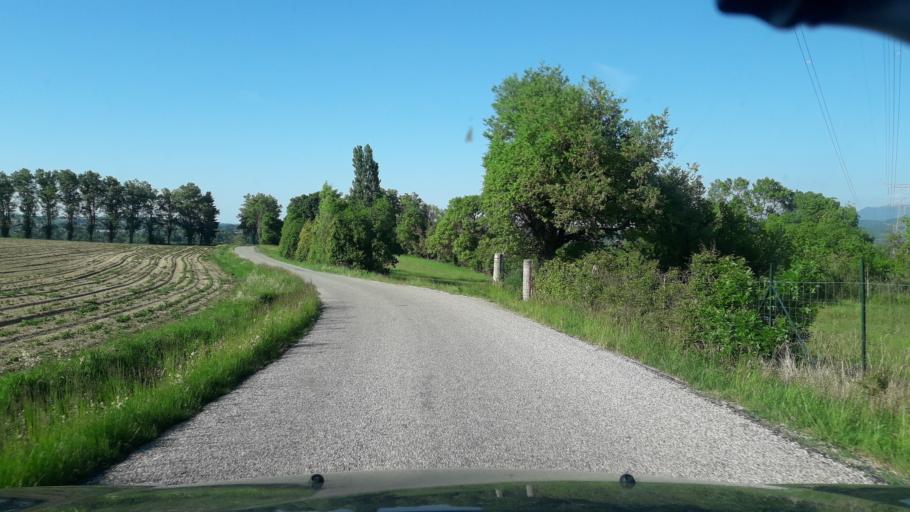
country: FR
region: Rhone-Alpes
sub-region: Departement de la Drome
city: Grane
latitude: 44.7368
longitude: 4.9008
